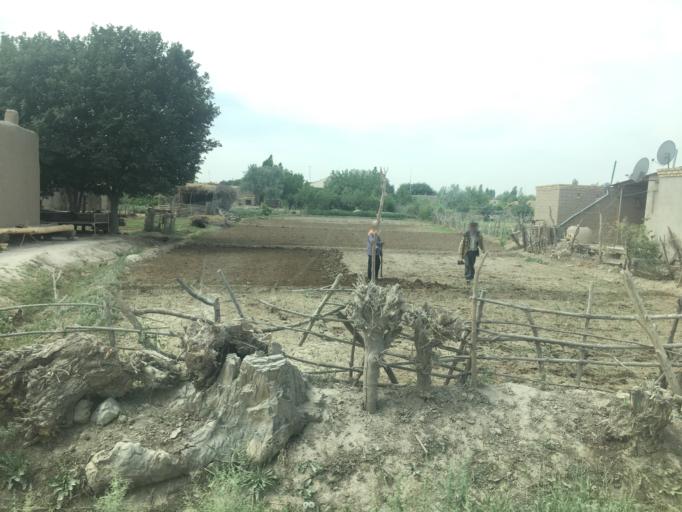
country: TM
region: Dasoguz
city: Tagta
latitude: 41.6007
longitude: 59.8492
